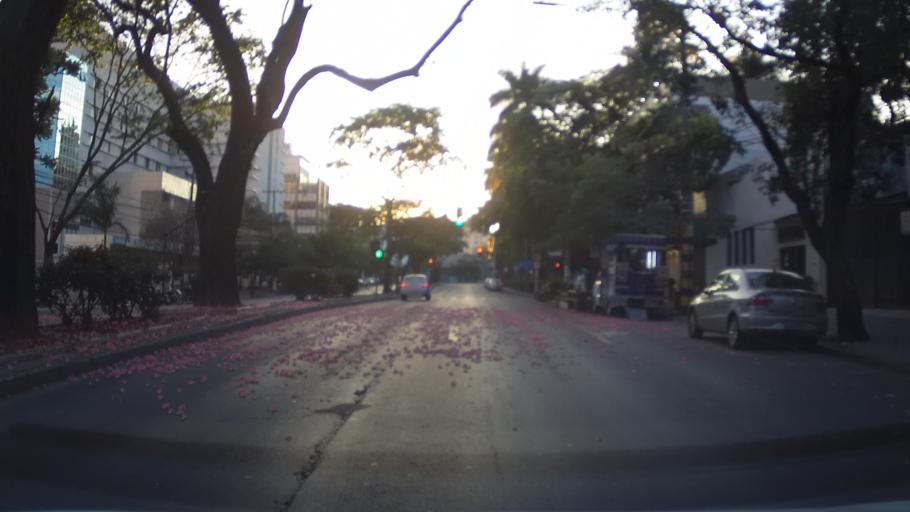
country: BR
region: Minas Gerais
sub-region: Belo Horizonte
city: Belo Horizonte
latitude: -19.9223
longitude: -43.9207
